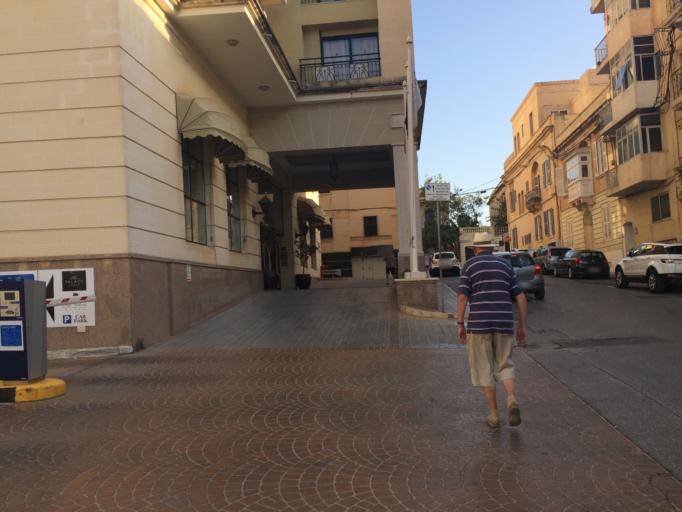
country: MT
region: Tas-Sliema
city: Sliema
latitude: 35.9129
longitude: 14.5027
